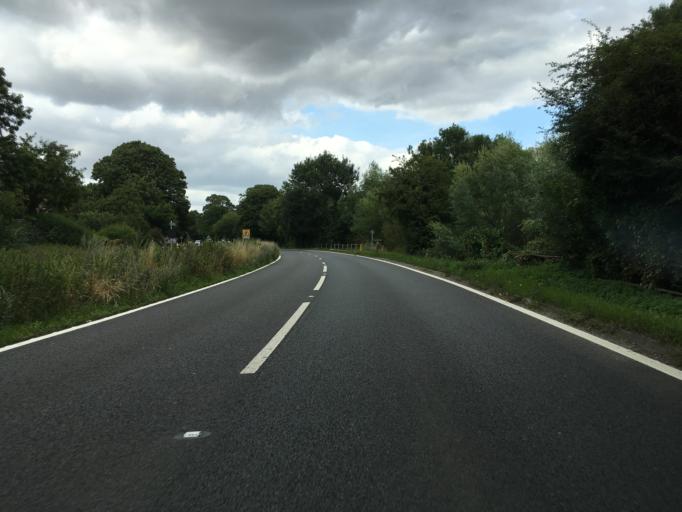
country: GB
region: England
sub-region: Hampshire
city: Kings Worthy
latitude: 51.0884
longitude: -1.2955
